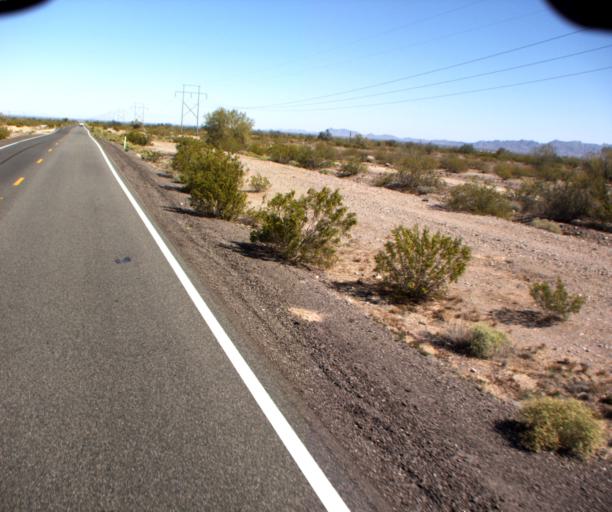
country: US
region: Arizona
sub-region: La Paz County
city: Quartzsite
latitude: 33.6049
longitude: -114.2170
